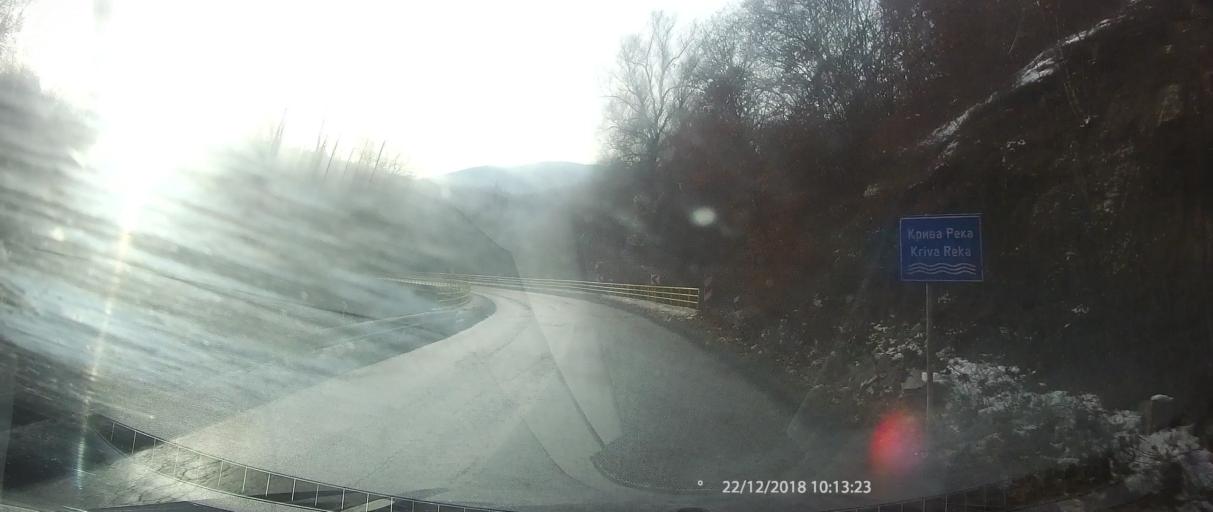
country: MK
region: Kratovo
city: Kratovo
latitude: 42.1738
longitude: 22.2239
